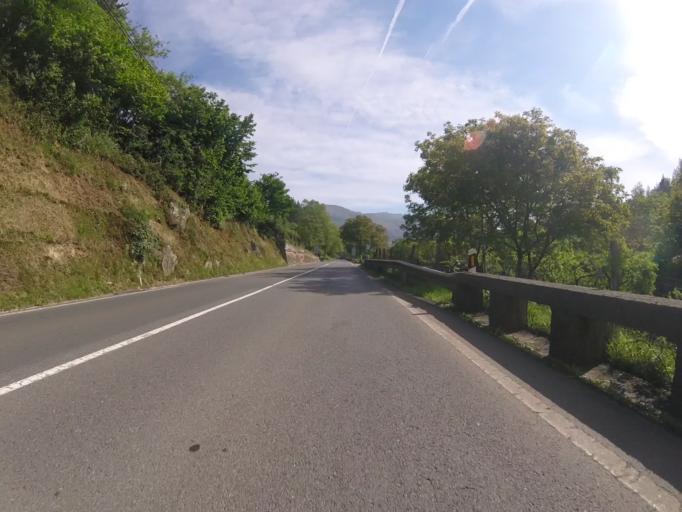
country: ES
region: Basque Country
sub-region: Provincia de Guipuzcoa
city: Azkoitia
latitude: 43.1649
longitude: -2.3308
